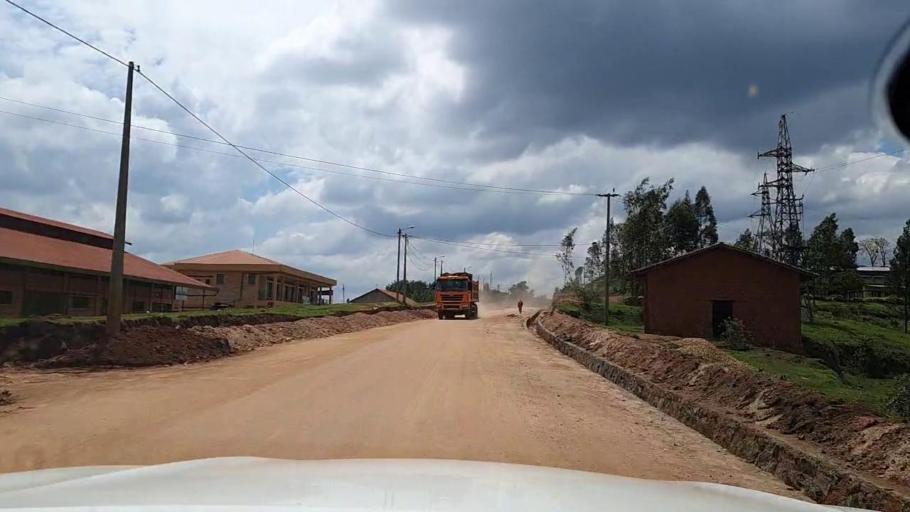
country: RW
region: Southern Province
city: Butare
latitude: -2.6918
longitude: 29.5682
